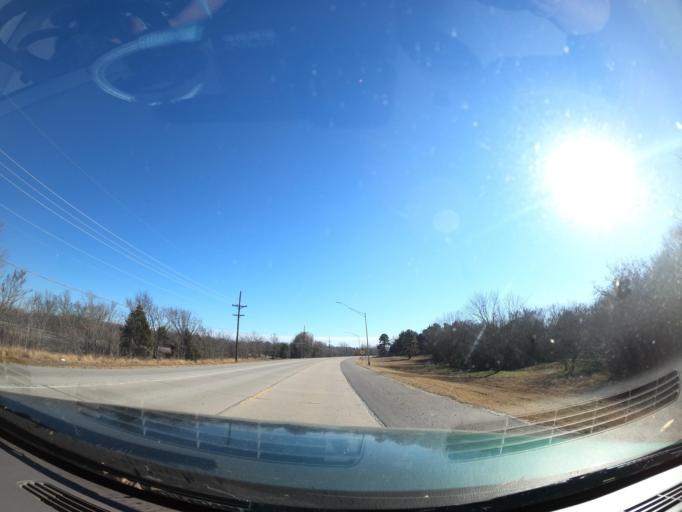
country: US
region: Oklahoma
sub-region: McIntosh County
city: Eufaula
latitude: 35.2982
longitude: -95.5831
